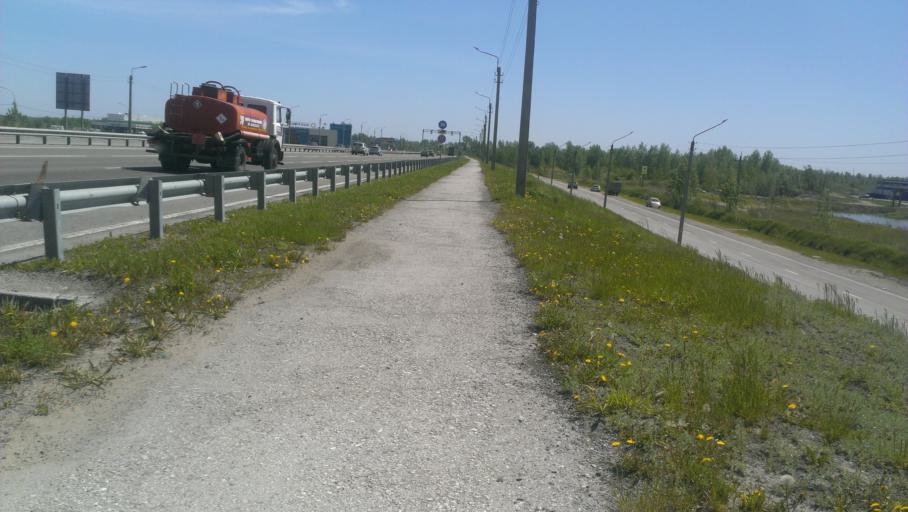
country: RU
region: Altai Krai
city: Zaton
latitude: 53.3179
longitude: 83.8193
